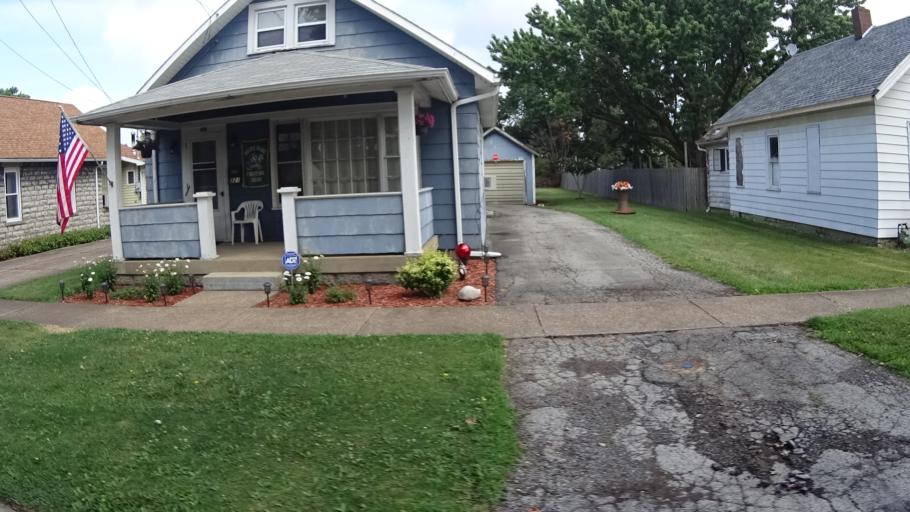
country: US
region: Ohio
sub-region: Erie County
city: Sandusky
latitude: 41.4348
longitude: -82.7040
